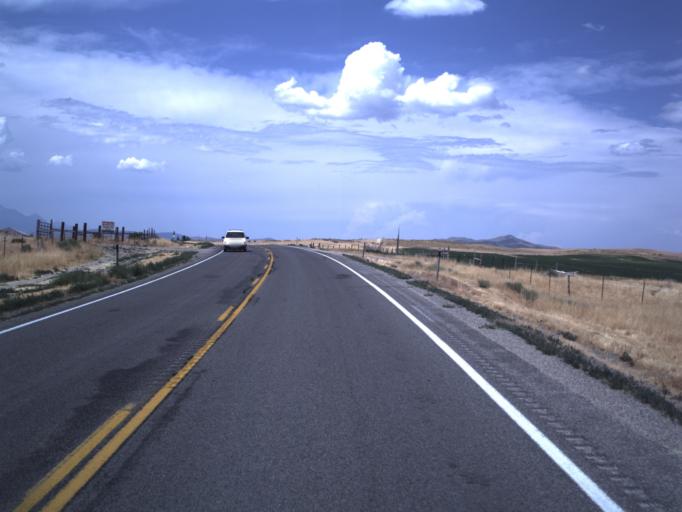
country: US
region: Utah
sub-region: Sanpete County
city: Moroni
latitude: 39.4937
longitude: -111.5632
